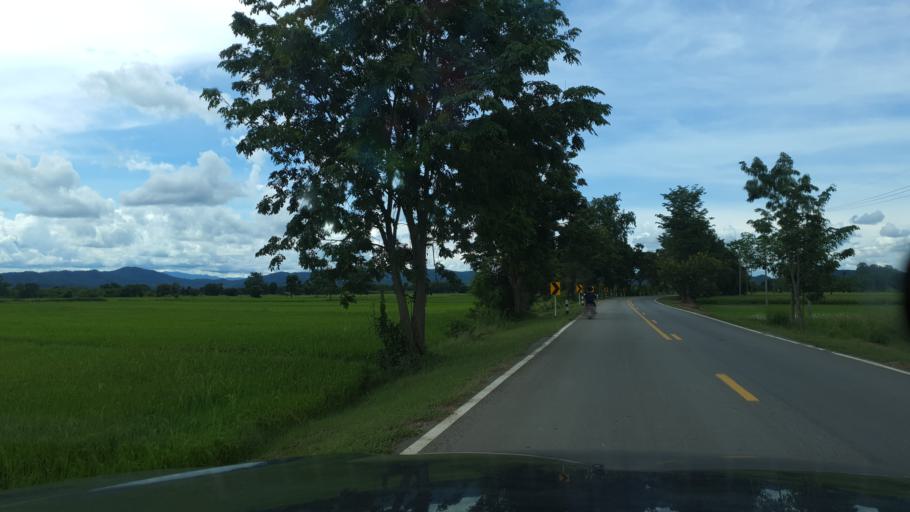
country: TH
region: Sukhothai
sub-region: Amphoe Si Satchanalai
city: Si Satchanalai
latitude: 17.4684
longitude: 99.7560
